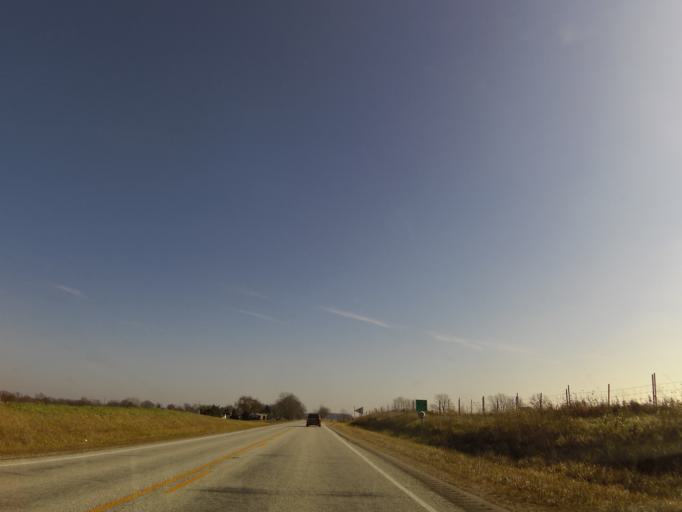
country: US
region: Indiana
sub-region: Shelby County
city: Morristown
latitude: 39.5694
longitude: -85.6304
